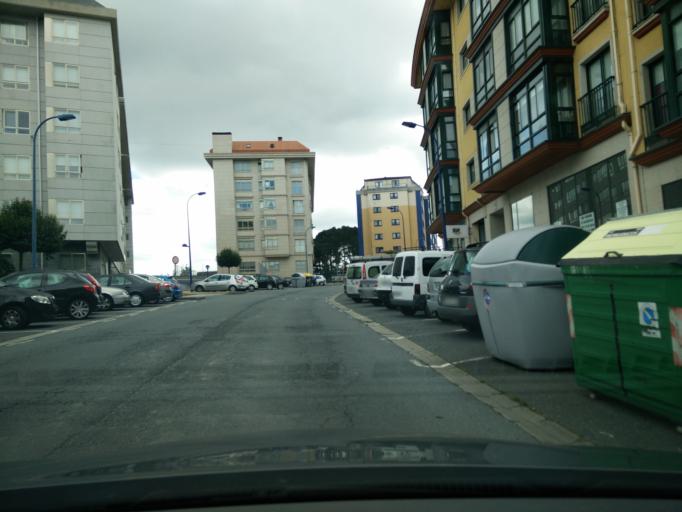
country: ES
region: Galicia
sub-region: Provincia da Coruna
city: Culleredo
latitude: 43.3216
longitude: -8.3802
